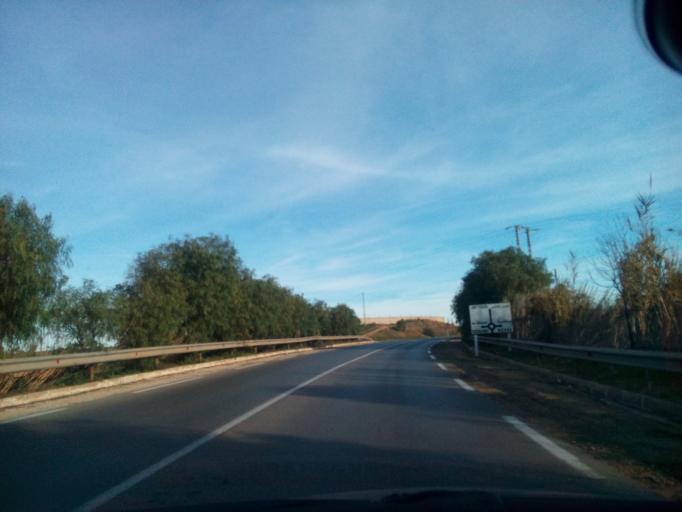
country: DZ
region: Mostaganem
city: Mostaganem
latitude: 35.8518
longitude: 0.1648
